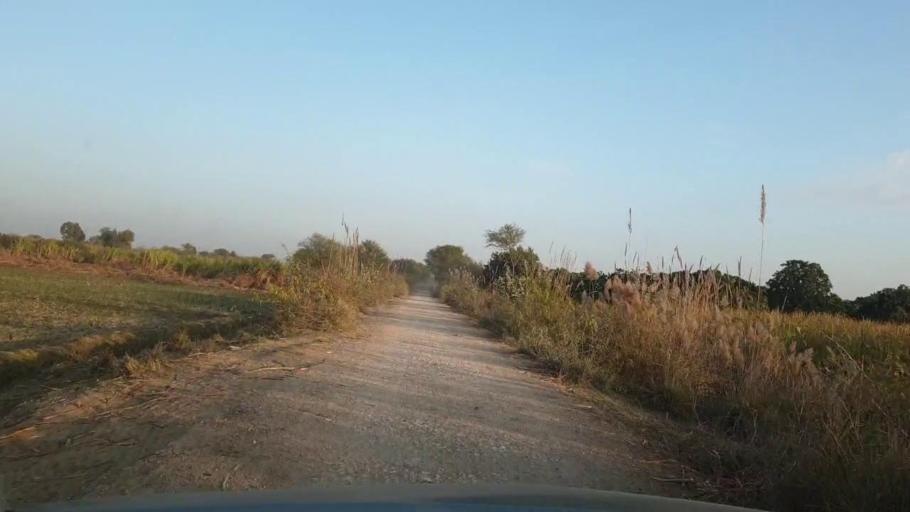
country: PK
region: Sindh
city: Matiari
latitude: 25.6138
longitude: 68.5340
